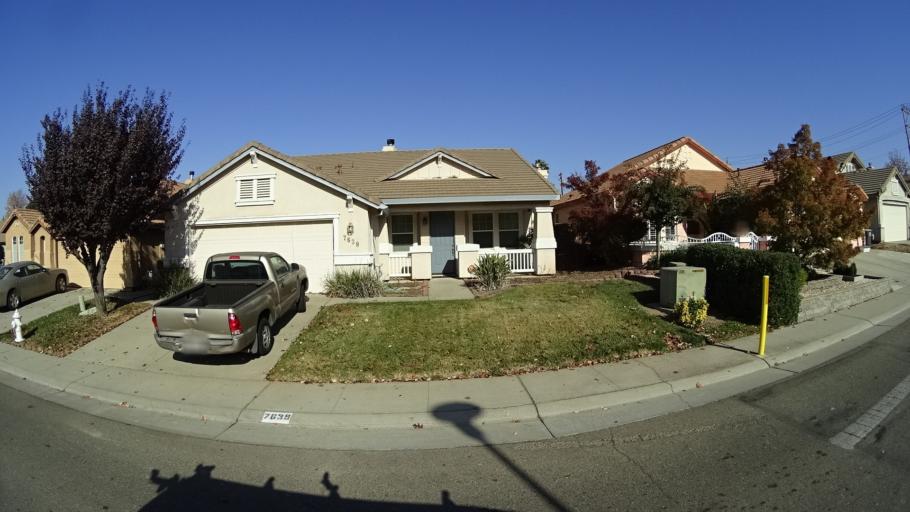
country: US
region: California
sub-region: Sacramento County
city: Citrus Heights
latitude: 38.6898
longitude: -121.2841
